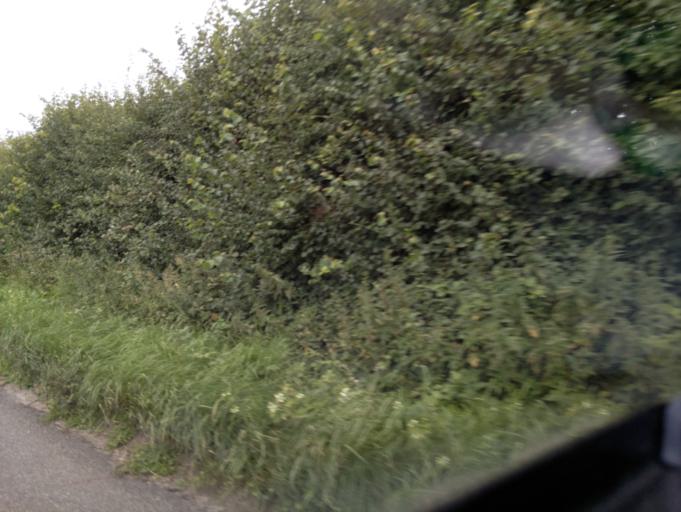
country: GB
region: England
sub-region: Somerset
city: Street
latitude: 51.1121
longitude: -2.7037
